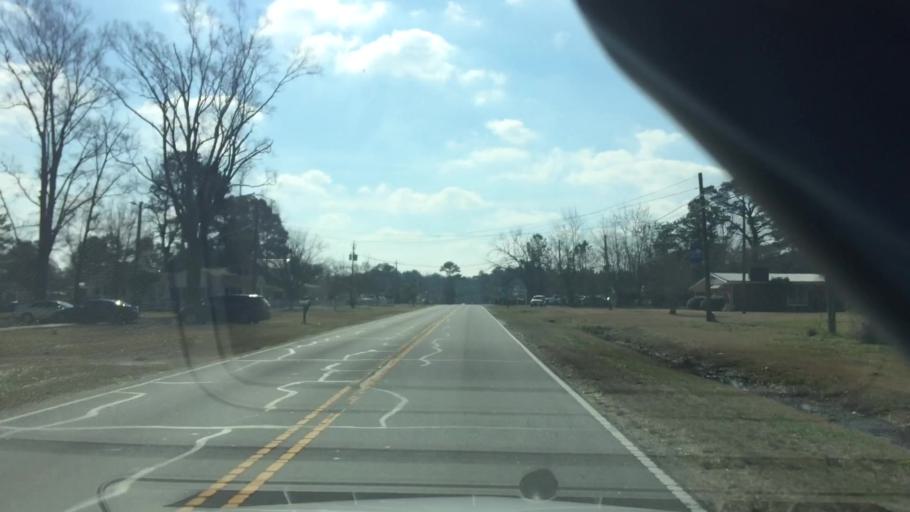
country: US
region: North Carolina
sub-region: Duplin County
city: Beulaville
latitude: 35.0656
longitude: -77.7385
